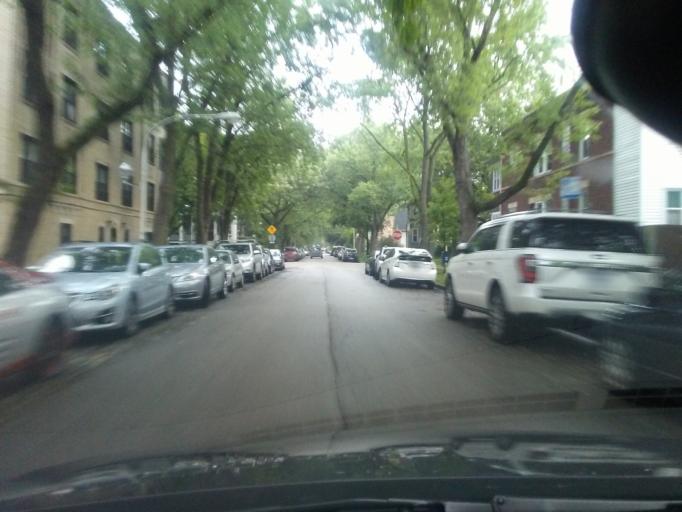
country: US
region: Illinois
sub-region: Cook County
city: Evanston
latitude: 42.0108
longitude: -87.6781
